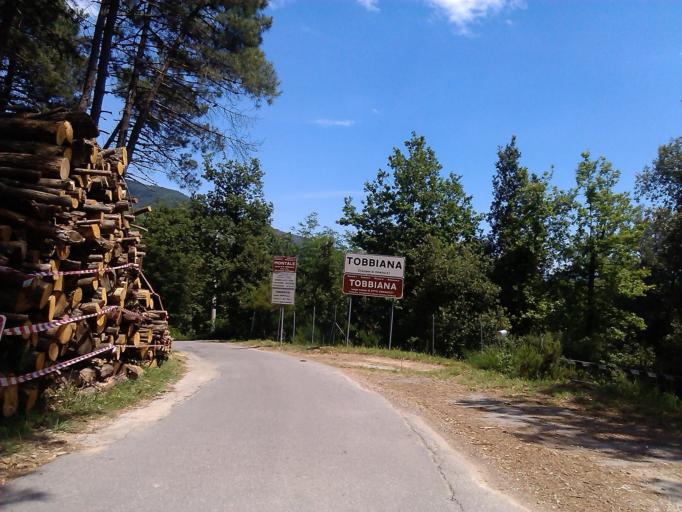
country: IT
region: Tuscany
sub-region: Provincia di Pistoia
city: Montale
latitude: 43.9676
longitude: 11.0394
